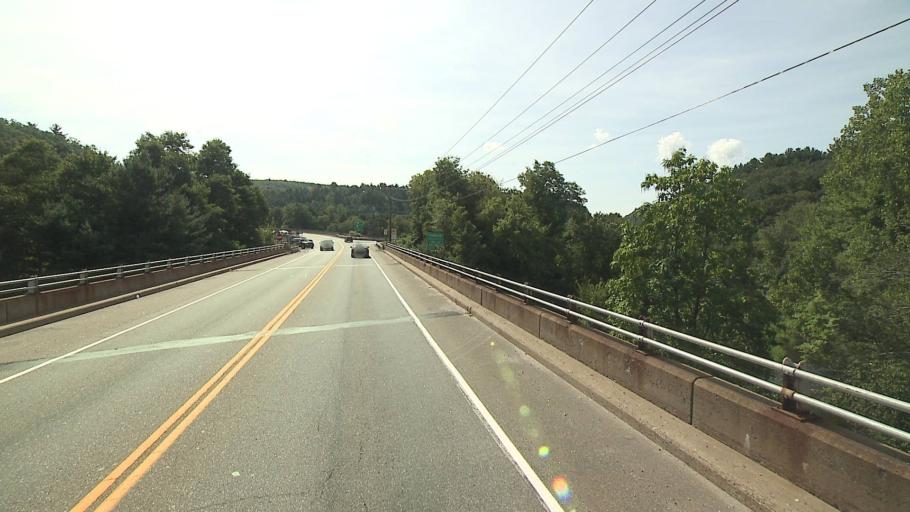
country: US
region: Connecticut
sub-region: Litchfield County
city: Torrington
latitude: 41.7635
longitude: -73.1171
